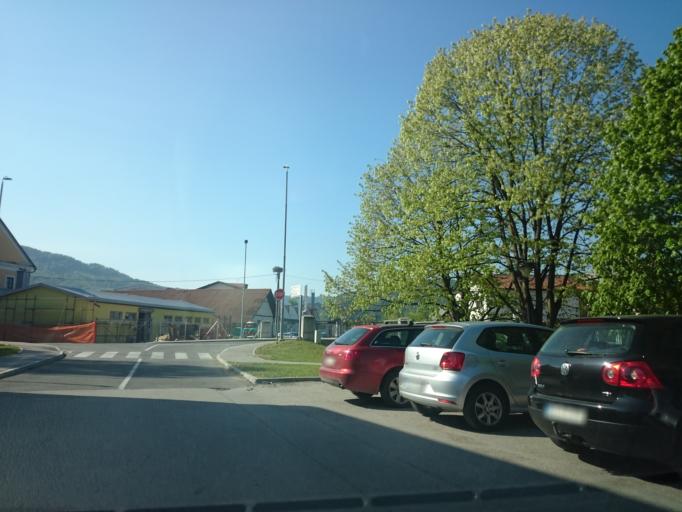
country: SI
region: Sentjur pri Celju
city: Sentjur
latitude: 46.2162
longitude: 15.3938
